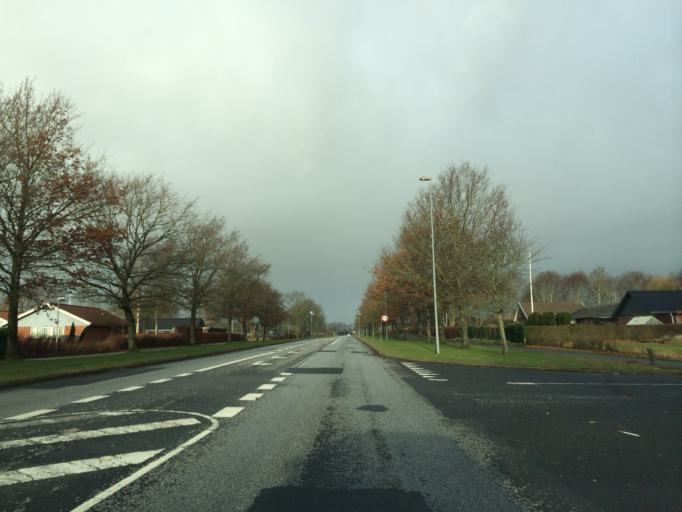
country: DK
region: Central Jutland
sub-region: Herning Kommune
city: Vildbjerg
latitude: 56.1892
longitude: 8.7644
